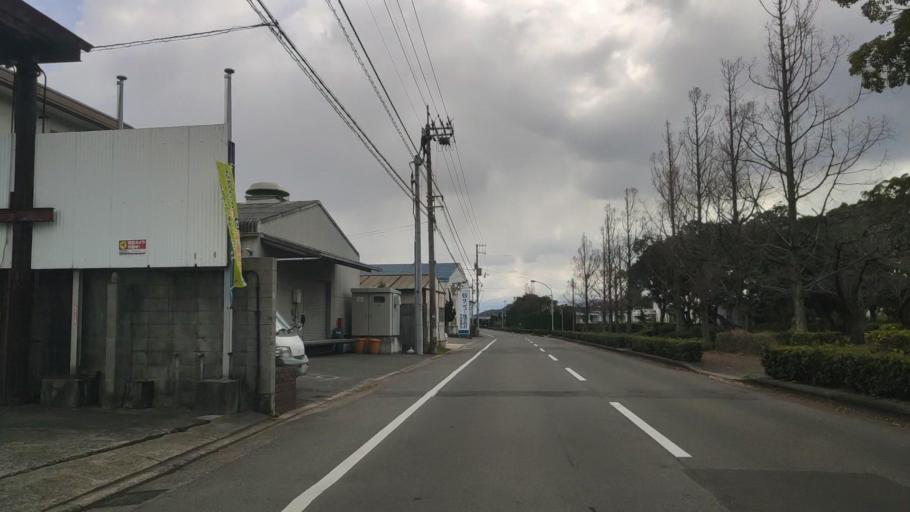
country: JP
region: Ehime
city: Saijo
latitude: 34.0556
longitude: 133.0215
